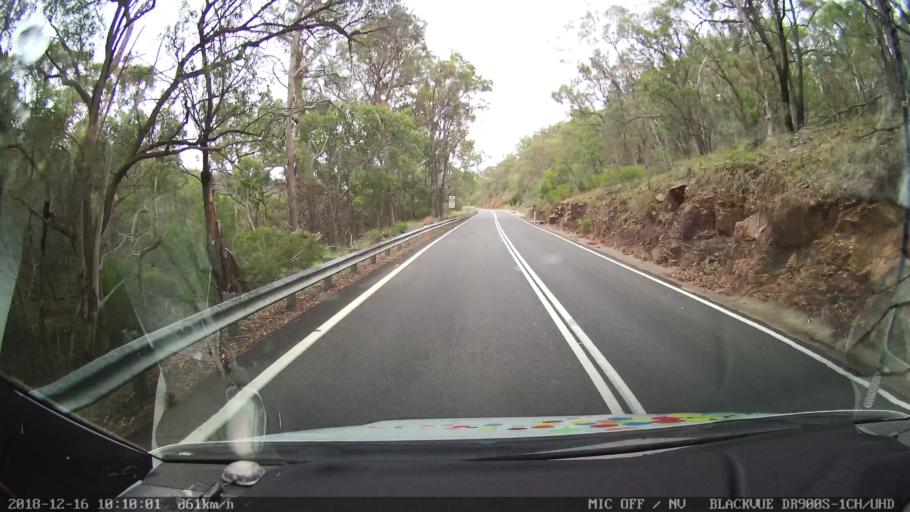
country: AU
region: New South Wales
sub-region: Glen Innes Severn
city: Glen Innes
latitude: -29.3203
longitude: 151.9210
